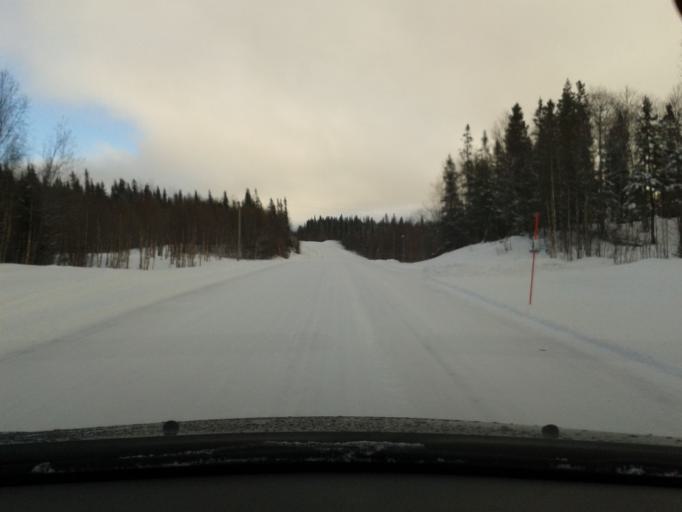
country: SE
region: Vaesterbotten
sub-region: Vilhelmina Kommun
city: Sjoberg
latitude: 65.2505
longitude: 15.5911
